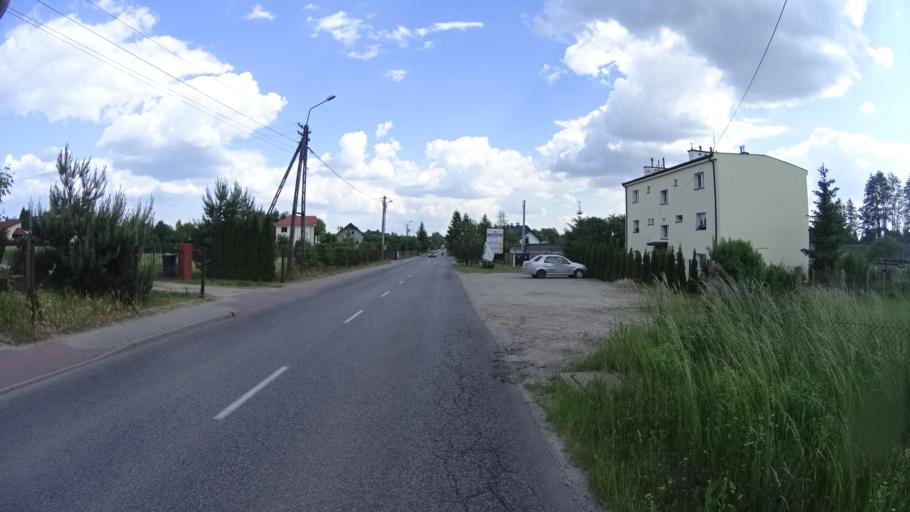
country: PL
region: Masovian Voivodeship
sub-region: Powiat piaseczynski
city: Tarczyn
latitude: 51.9876
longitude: 20.8259
